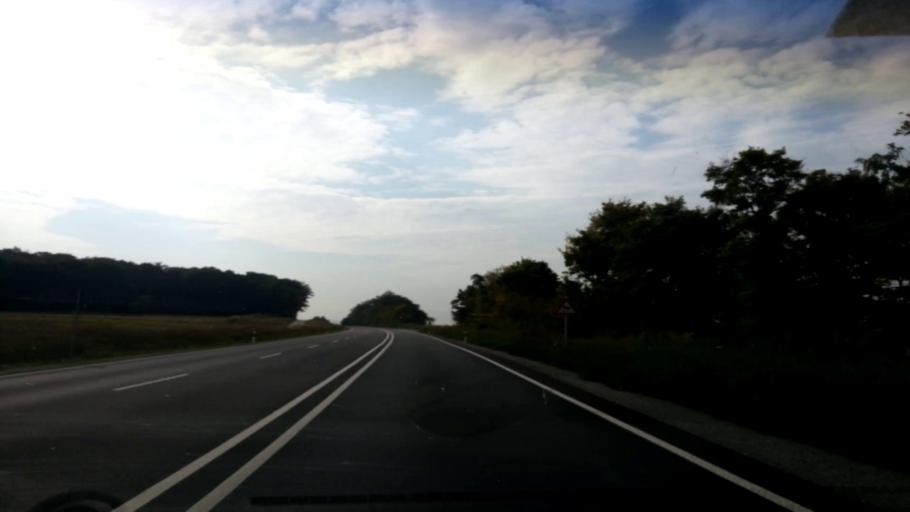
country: DE
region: Bavaria
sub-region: Regierungsbezirk Unterfranken
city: Gerolzhofen
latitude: 49.8843
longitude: 10.3562
